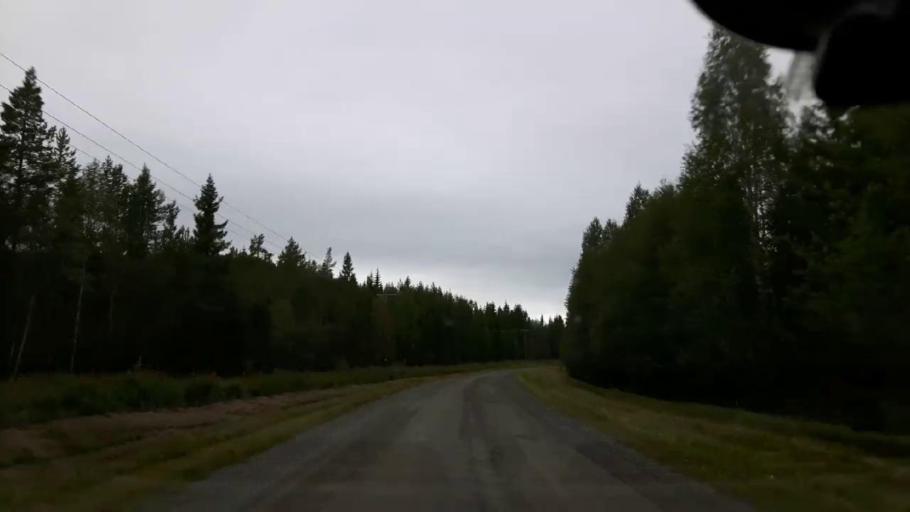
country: SE
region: Vaesternorrland
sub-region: Ange Kommun
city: Fransta
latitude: 62.8608
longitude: 15.9883
